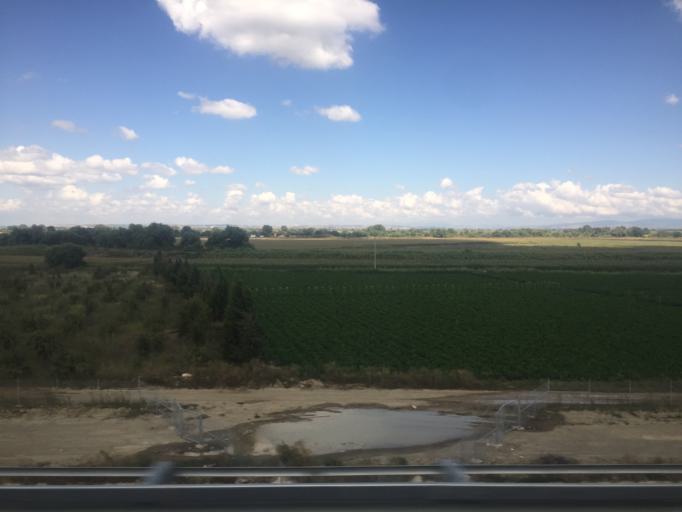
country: TR
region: Bursa
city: Karacabey
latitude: 40.1243
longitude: 28.2840
